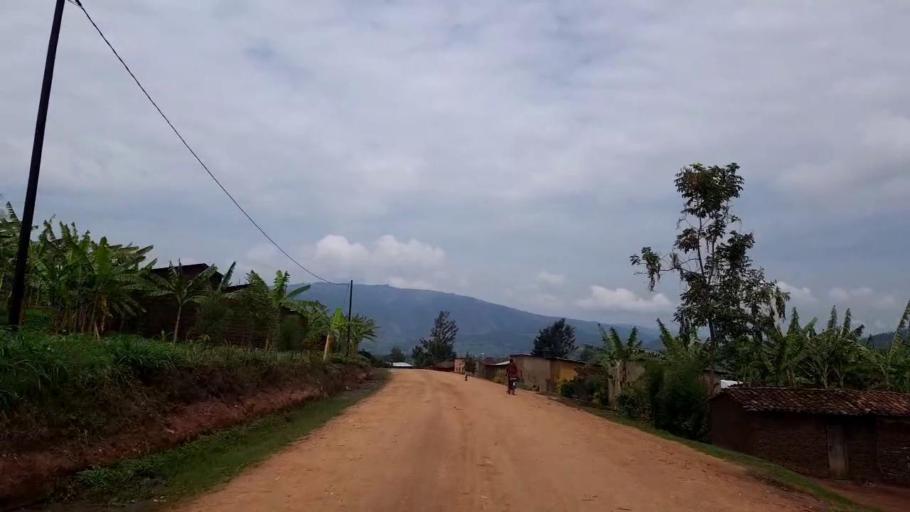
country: RW
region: Northern Province
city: Byumba
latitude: -1.4975
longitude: 30.2254
